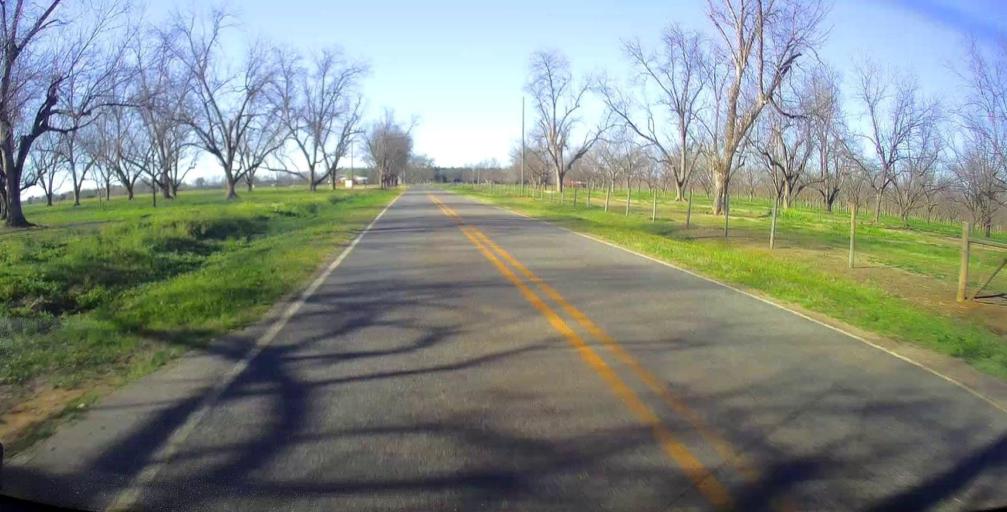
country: US
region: Georgia
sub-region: Peach County
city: Fort Valley
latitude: 32.6170
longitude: -83.8522
